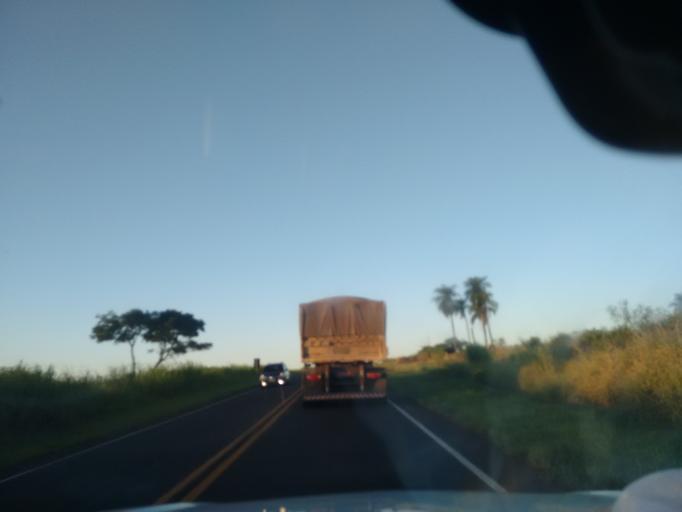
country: BR
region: Mato Grosso do Sul
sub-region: Eldorado
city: Eldorado
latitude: -23.5735
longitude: -54.1960
